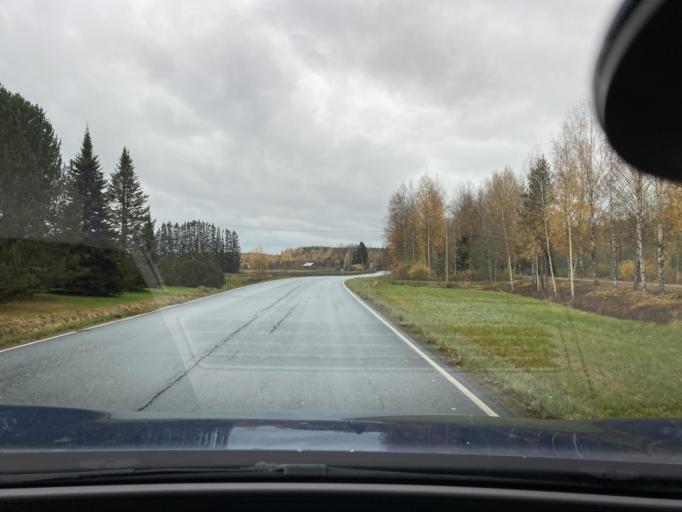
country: FI
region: Satakunta
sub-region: Pori
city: Kokemaeki
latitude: 61.2609
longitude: 22.3987
